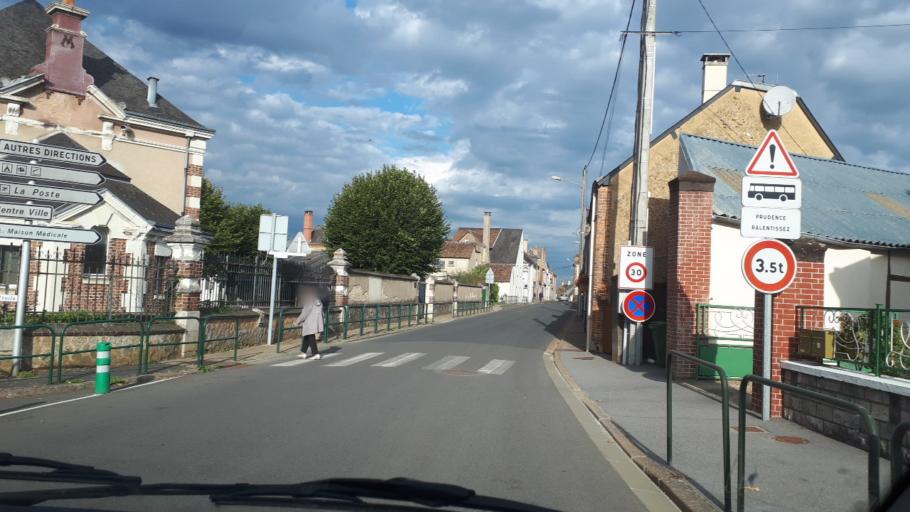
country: FR
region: Centre
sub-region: Departement du Loir-et-Cher
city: Mondoubleau
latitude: 47.9798
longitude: 0.8984
